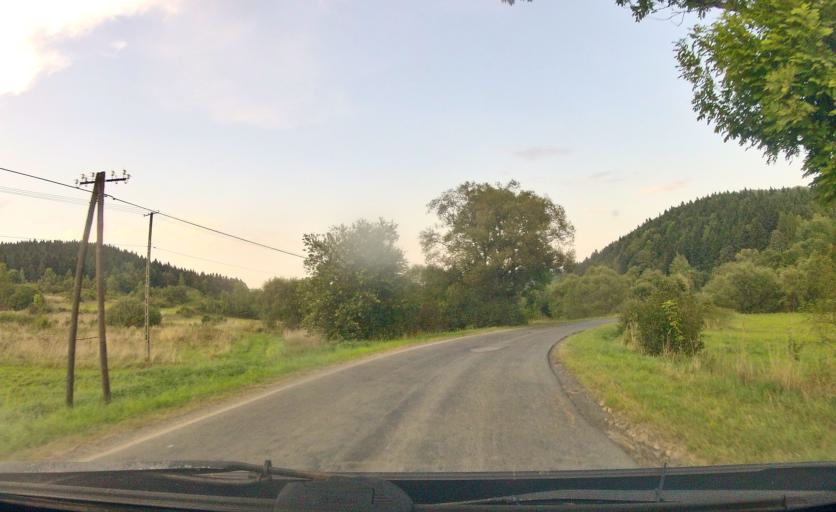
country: PL
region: Subcarpathian Voivodeship
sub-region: Powiat krosnienski
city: Dukla
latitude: 49.5416
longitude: 21.6170
